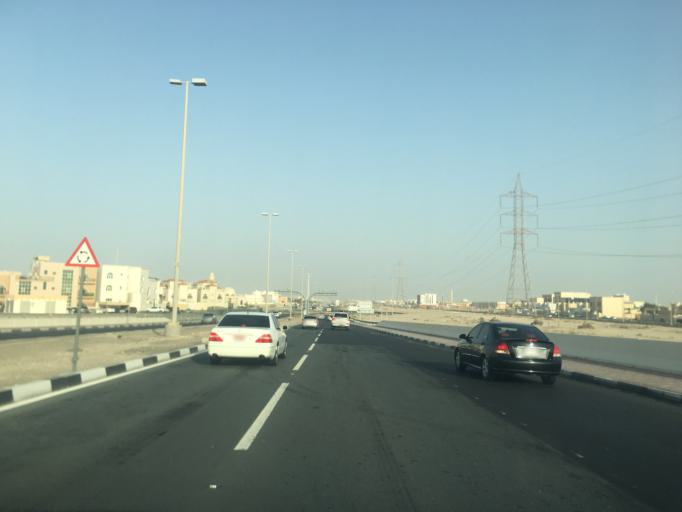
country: AE
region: Abu Dhabi
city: Abu Dhabi
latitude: 24.3243
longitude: 54.6252
